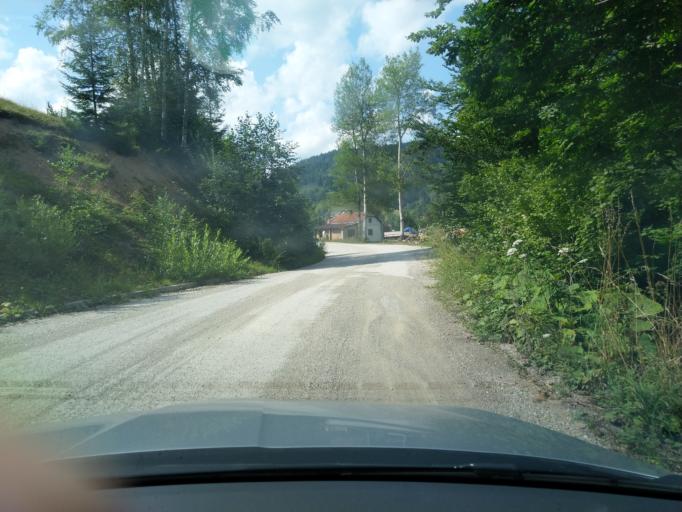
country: RS
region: Central Serbia
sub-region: Zlatiborski Okrug
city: Nova Varos
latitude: 43.5809
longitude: 19.8820
